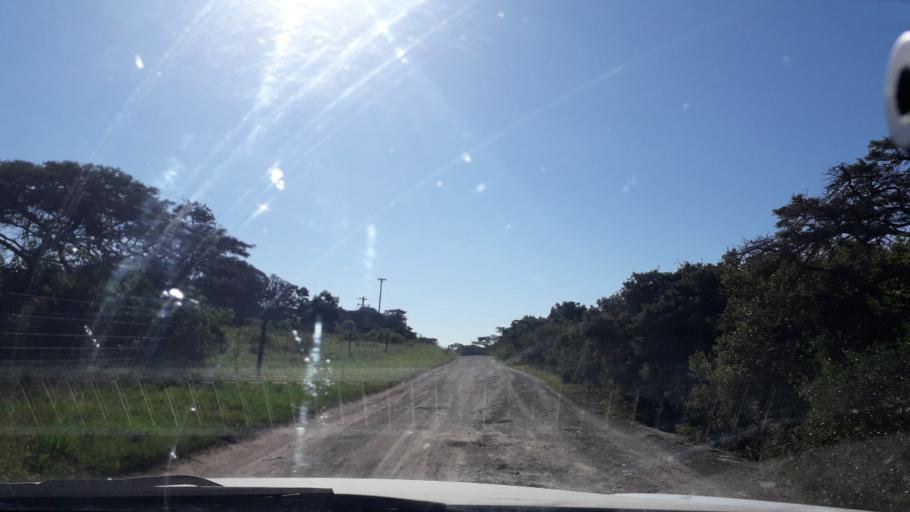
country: ZA
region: Eastern Cape
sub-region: Buffalo City Metropolitan Municipality
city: East London
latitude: -32.8434
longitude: 27.9721
